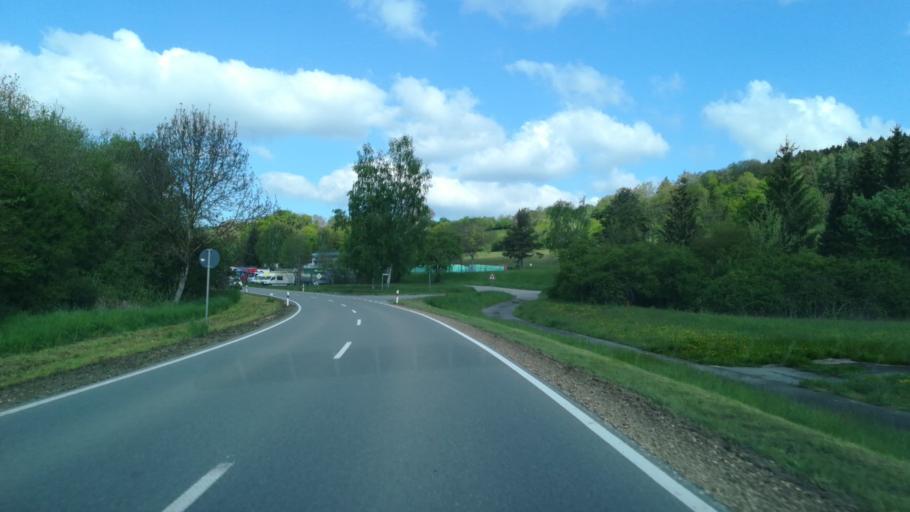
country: DE
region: Baden-Wuerttemberg
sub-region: Freiburg Region
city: Tengen
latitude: 47.7986
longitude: 8.7056
